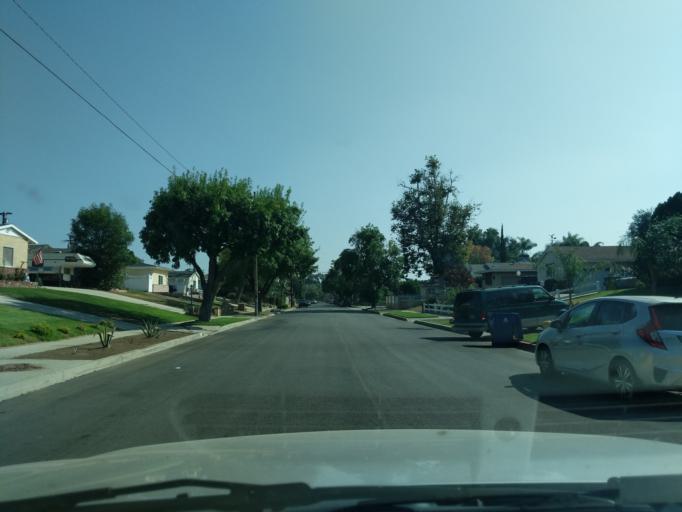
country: US
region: California
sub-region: Los Angeles County
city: San Fernando
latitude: 34.2701
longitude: -118.4593
